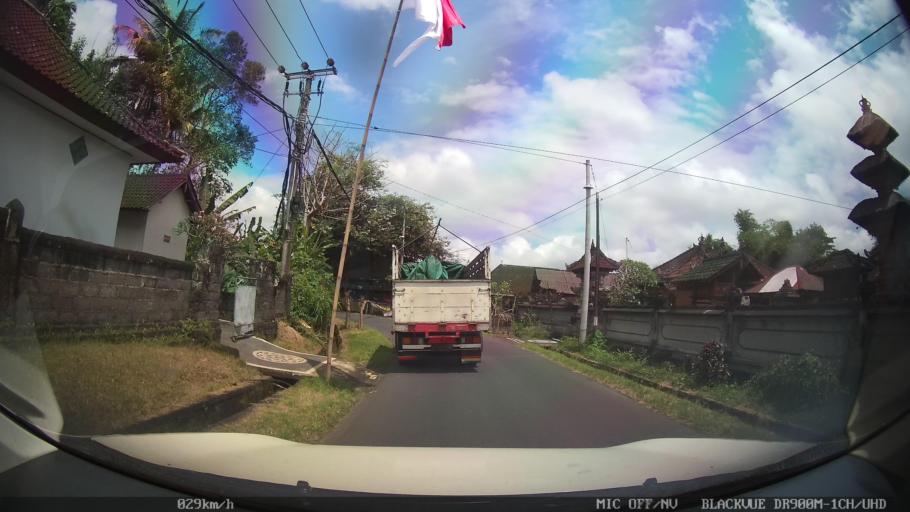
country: ID
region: Bali
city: Banjar Kelodan
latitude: -8.4882
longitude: 115.3673
